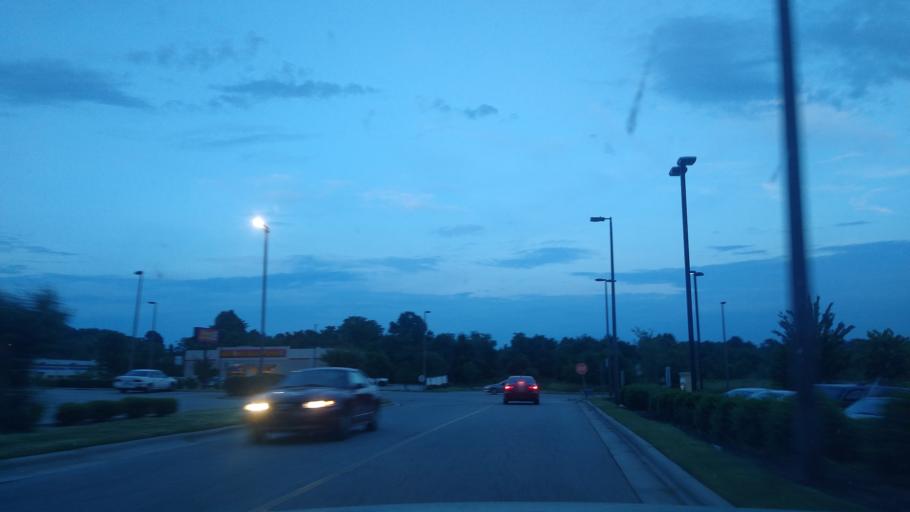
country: US
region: North Carolina
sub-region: Guilford County
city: Greensboro
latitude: 36.1119
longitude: -79.7549
